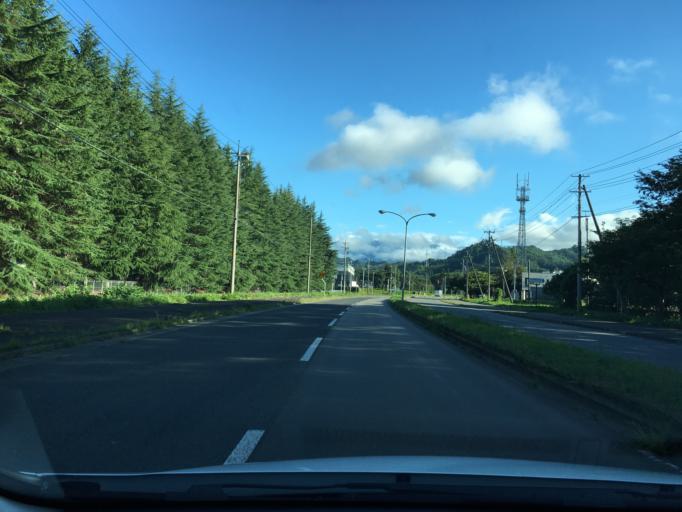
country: JP
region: Yamagata
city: Yonezawa
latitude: 37.9051
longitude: 140.1667
